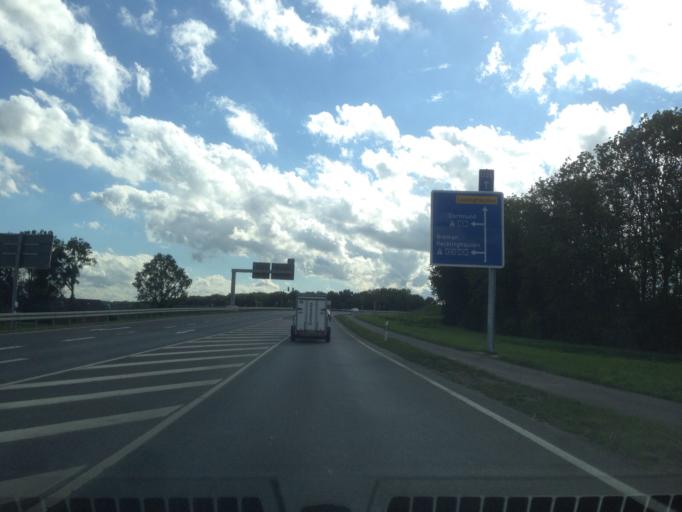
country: DE
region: North Rhine-Westphalia
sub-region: Regierungsbezirk Munster
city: Senden
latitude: 51.8894
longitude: 7.5772
